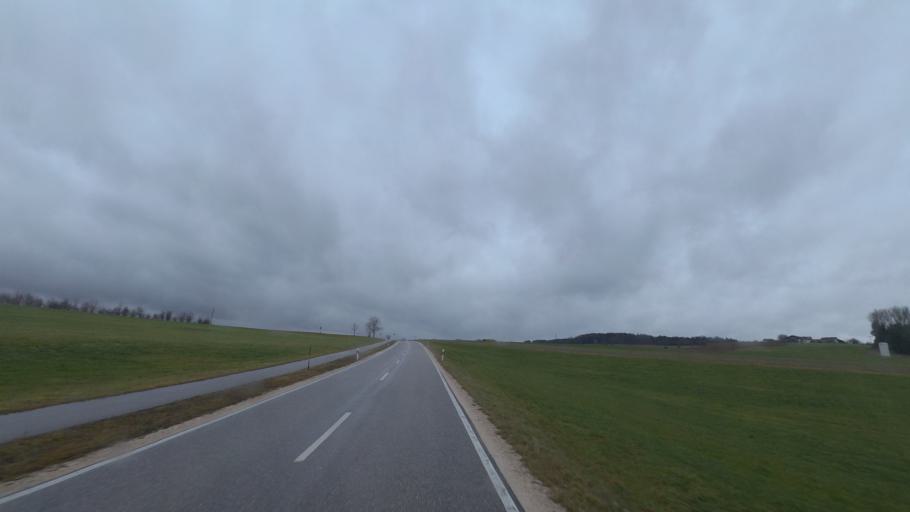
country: DE
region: Bavaria
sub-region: Upper Bavaria
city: Taching am See
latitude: 47.9556
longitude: 12.7775
